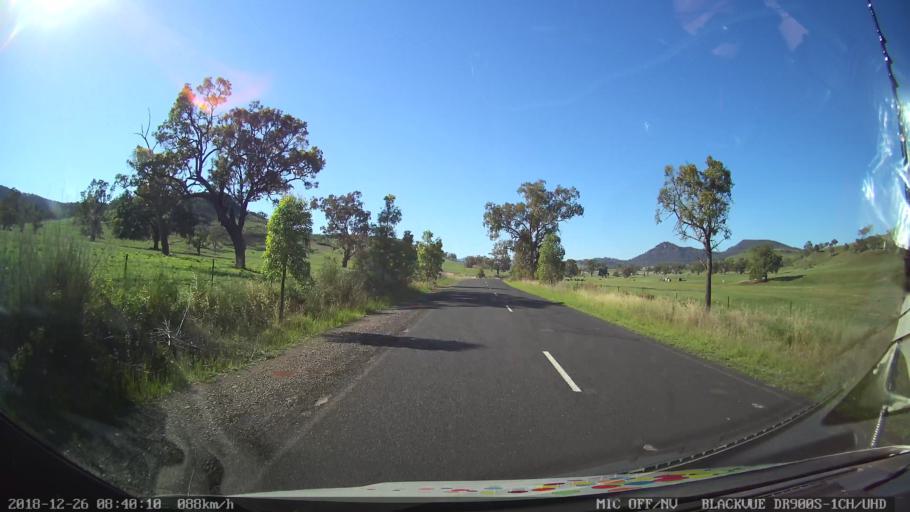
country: AU
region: New South Wales
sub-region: Mid-Western Regional
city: Kandos
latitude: -32.4632
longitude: 150.0760
